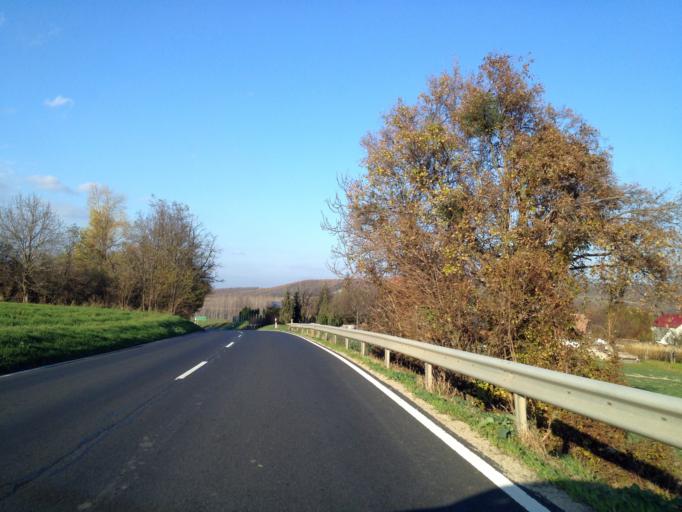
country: HU
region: Gyor-Moson-Sopron
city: Bakonyszentlaszlo
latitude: 47.3632
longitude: 17.8745
